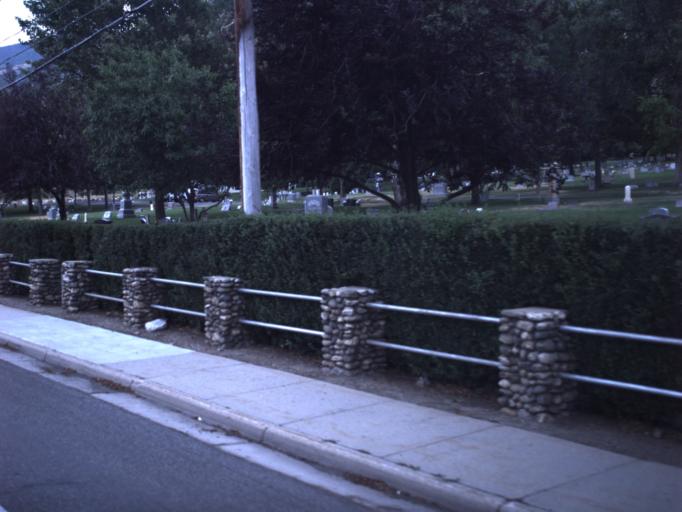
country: US
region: Utah
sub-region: Davis County
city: Farmington
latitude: 40.9713
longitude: -111.8833
